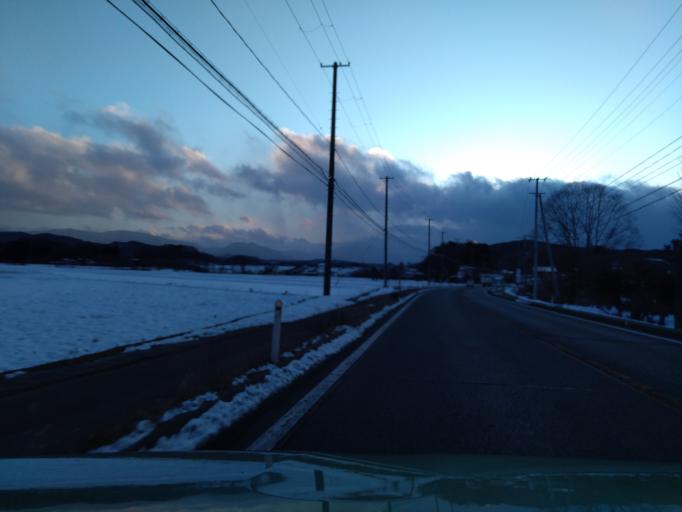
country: JP
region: Iwate
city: Shizukuishi
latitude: 39.6935
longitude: 141.0165
